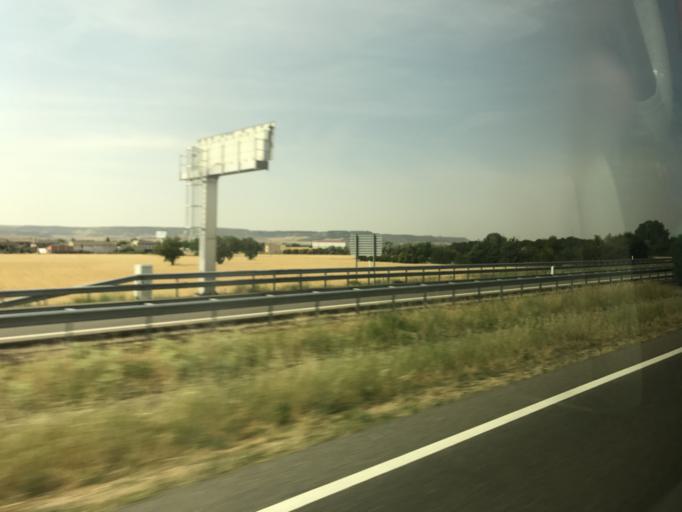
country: ES
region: Castille and Leon
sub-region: Provincia de Palencia
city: Villodrigo
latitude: 42.1491
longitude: -4.0963
